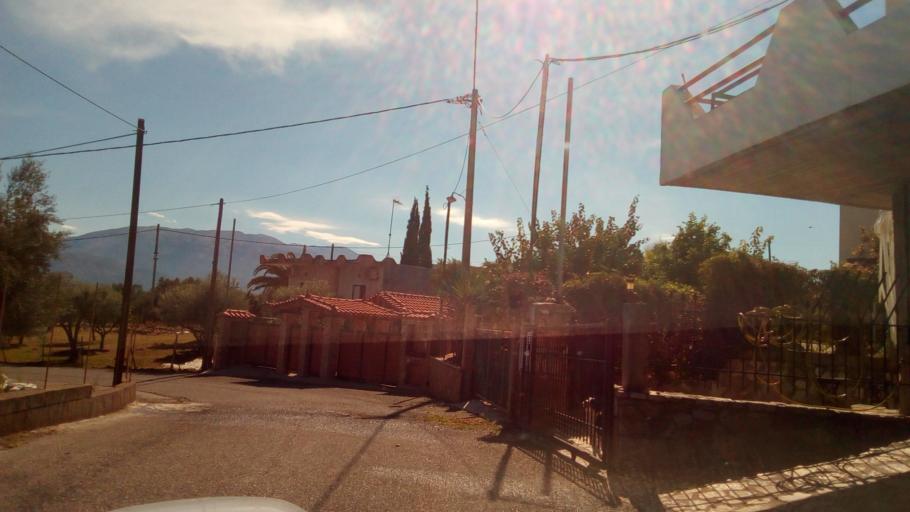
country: GR
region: West Greece
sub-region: Nomos Aitolias kai Akarnanias
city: Antirrio
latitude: 38.3696
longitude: 21.7741
